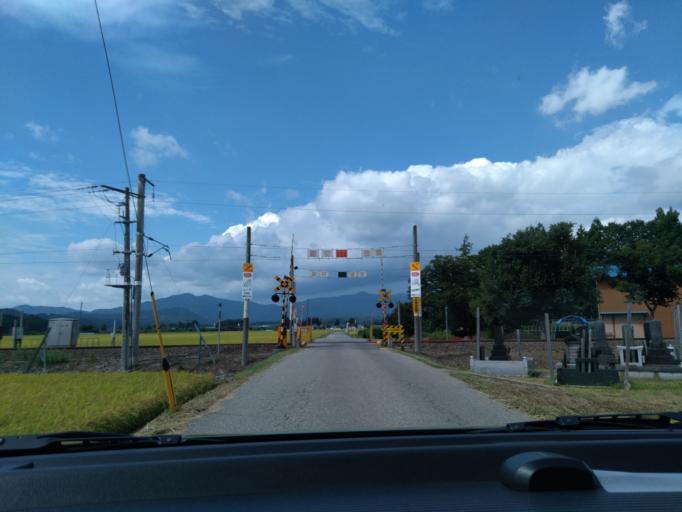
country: JP
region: Akita
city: Kakunodatemachi
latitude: 39.6044
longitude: 140.5864
